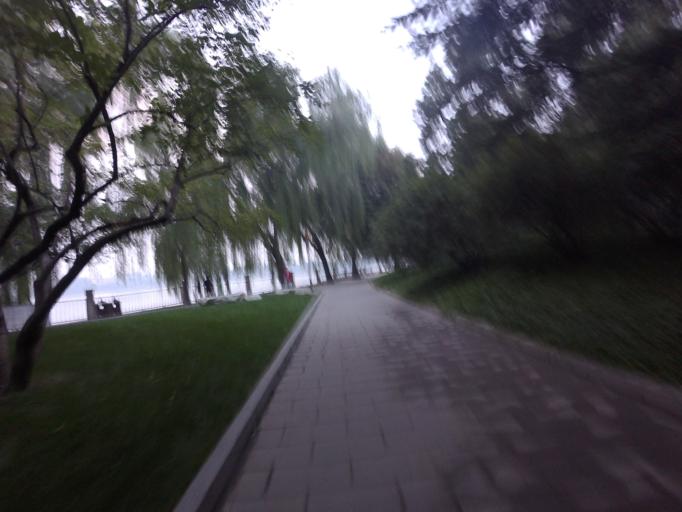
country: CN
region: Beijing
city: Jingshan
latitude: 39.9267
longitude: 116.3856
